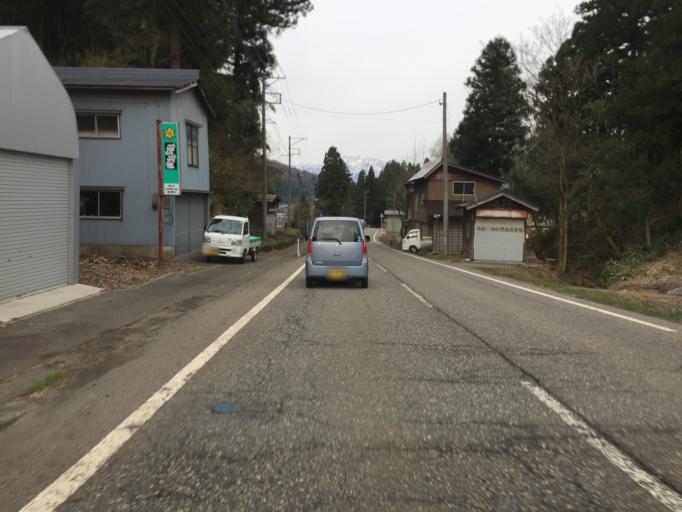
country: JP
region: Niigata
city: Tochio-honcho
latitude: 37.5047
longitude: 139.0310
